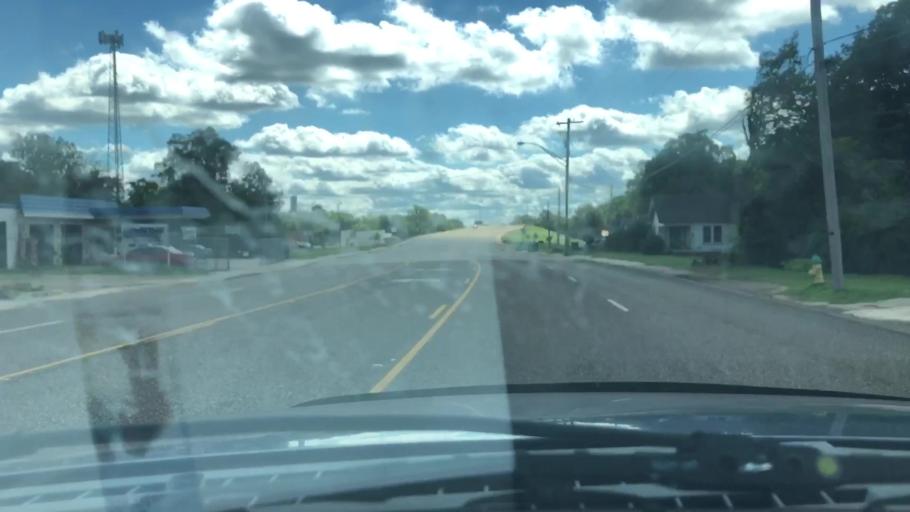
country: US
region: Texas
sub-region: Bowie County
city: Texarkana
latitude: 33.4181
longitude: -94.0612
